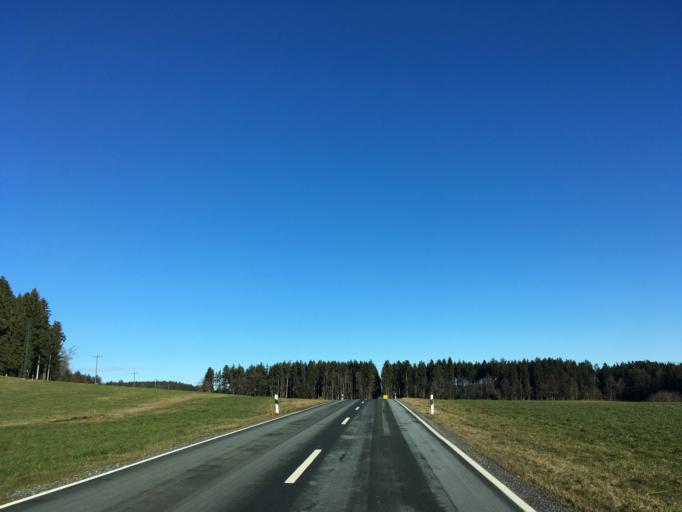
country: DE
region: Bavaria
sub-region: Upper Bavaria
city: Hoslwang
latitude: 47.9543
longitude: 12.3535
